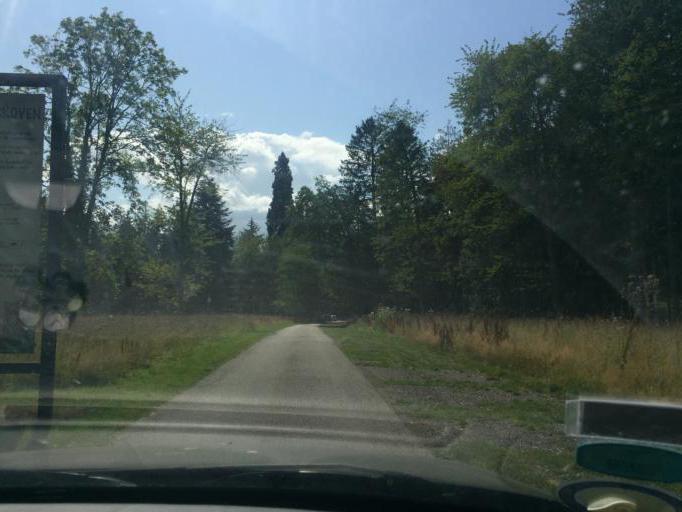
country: DK
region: Zealand
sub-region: Lolland Kommune
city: Maribo
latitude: 54.8225
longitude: 11.4886
